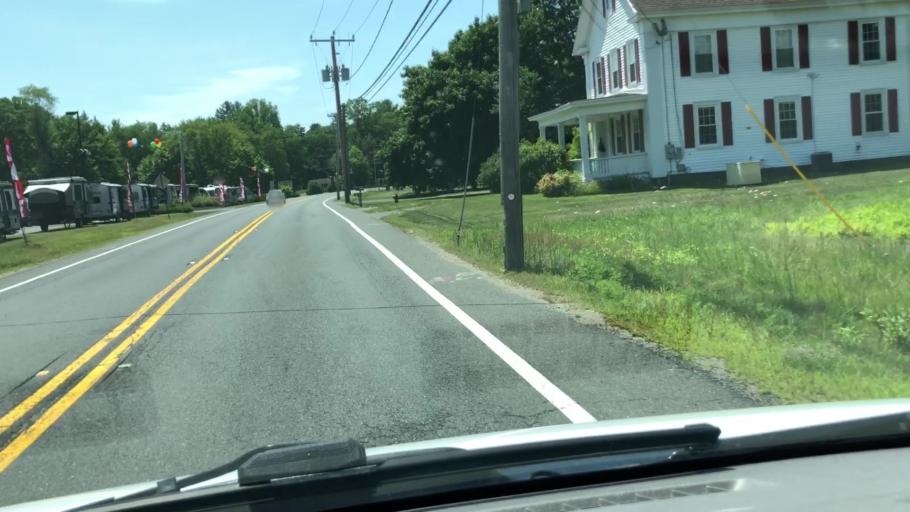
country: US
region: Massachusetts
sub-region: Franklin County
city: Whately
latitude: 42.4261
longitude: -72.6219
